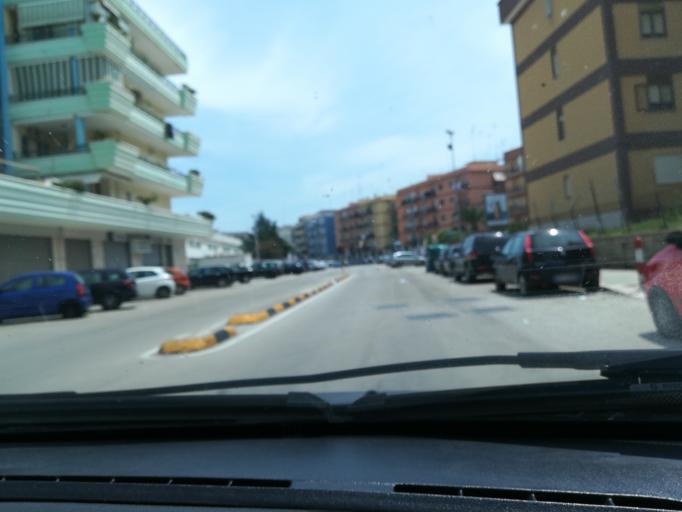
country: IT
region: Apulia
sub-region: Provincia di Barletta - Andria - Trani
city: Barletta
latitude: 41.3229
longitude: 16.2684
